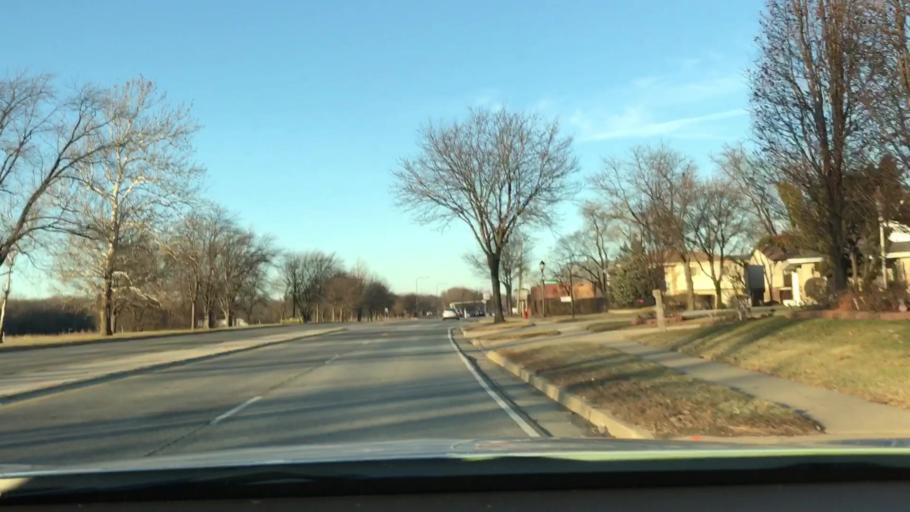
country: US
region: Illinois
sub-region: Cook County
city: Elk Grove Village
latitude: 42.0247
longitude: -87.9883
